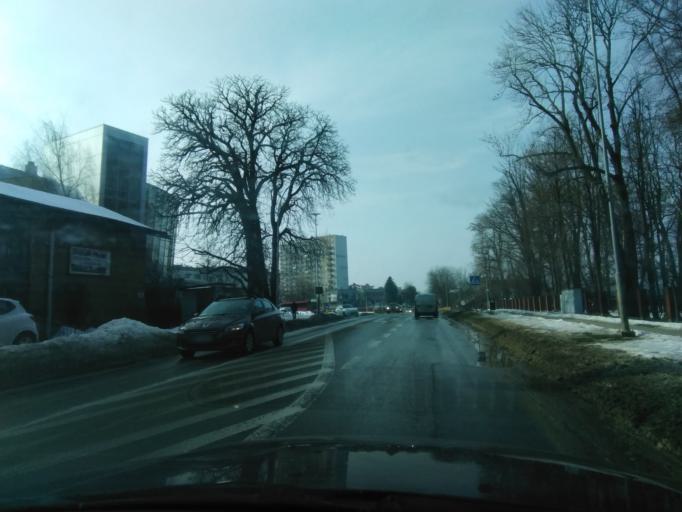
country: PL
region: Subcarpathian Voivodeship
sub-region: Krosno
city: Krosno
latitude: 49.6965
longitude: 21.7557
